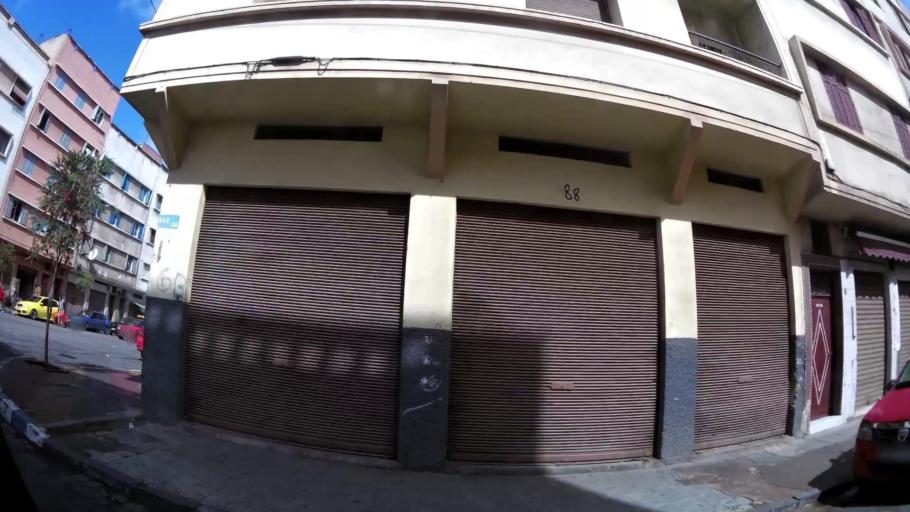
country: MA
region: Grand Casablanca
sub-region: Casablanca
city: Casablanca
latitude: 33.5642
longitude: -7.5894
